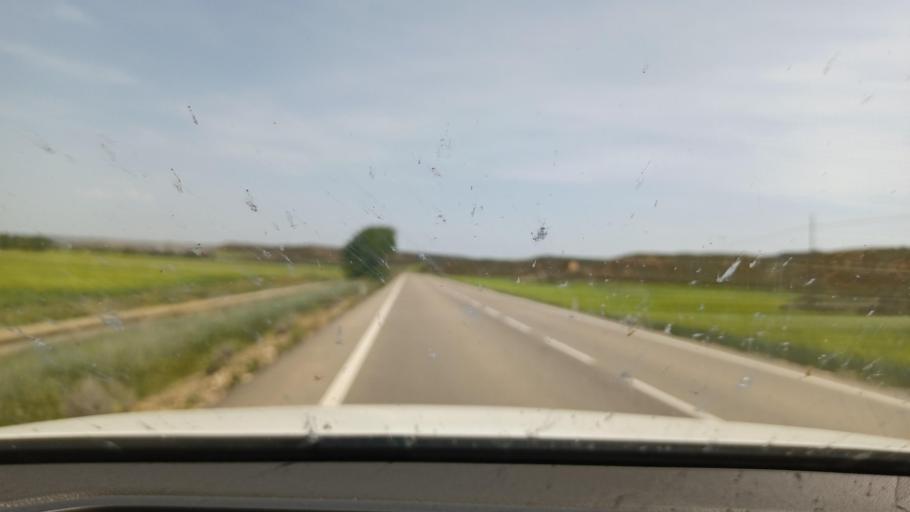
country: ES
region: Aragon
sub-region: Provincia de Zaragoza
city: Pozuel de Ariza
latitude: 41.3253
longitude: -2.1461
